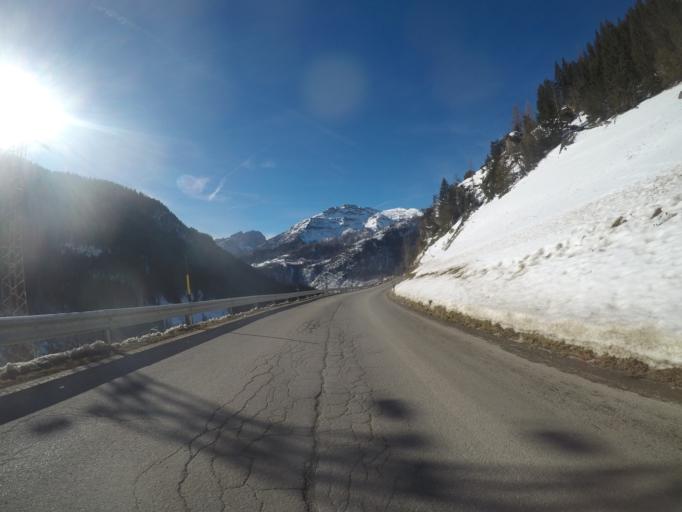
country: IT
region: Veneto
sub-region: Provincia di Belluno
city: Livinallongo del Col di Lana
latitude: 46.4822
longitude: 11.9817
